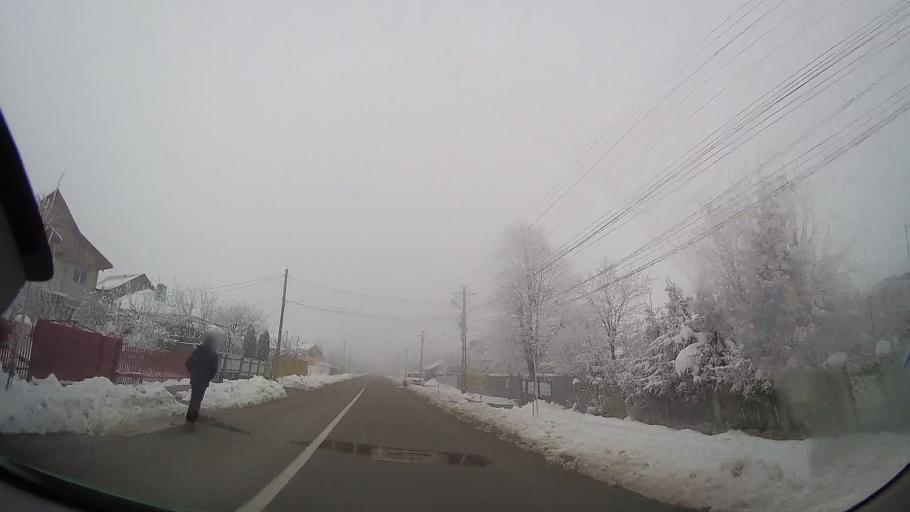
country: RO
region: Iasi
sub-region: Municipiul Pascani
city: Pascani
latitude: 47.2581
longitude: 26.7143
